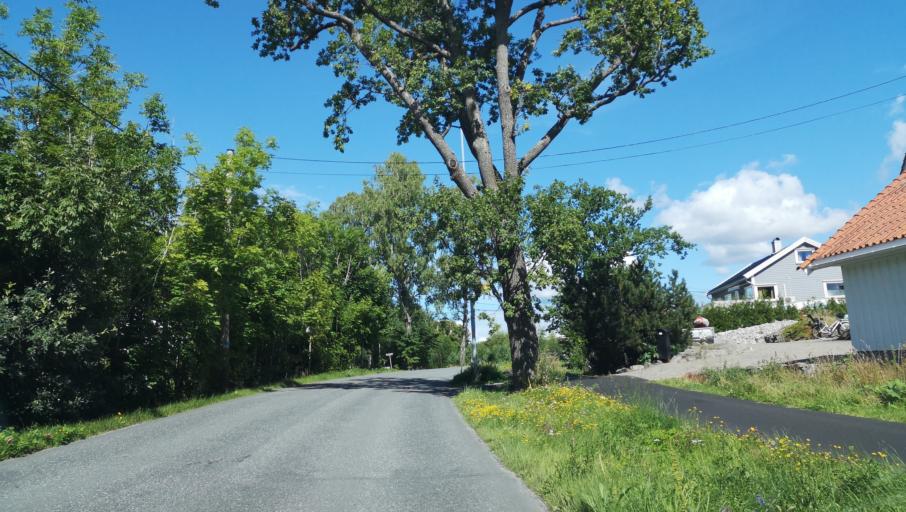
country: NO
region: Akershus
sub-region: Frogn
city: Drobak
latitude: 59.6599
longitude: 10.6395
